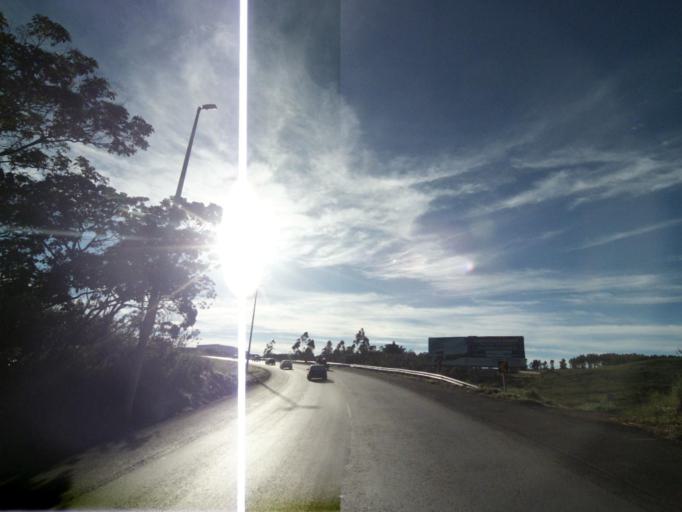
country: BR
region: Federal District
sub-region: Brasilia
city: Brasilia
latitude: -15.7895
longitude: -48.2258
